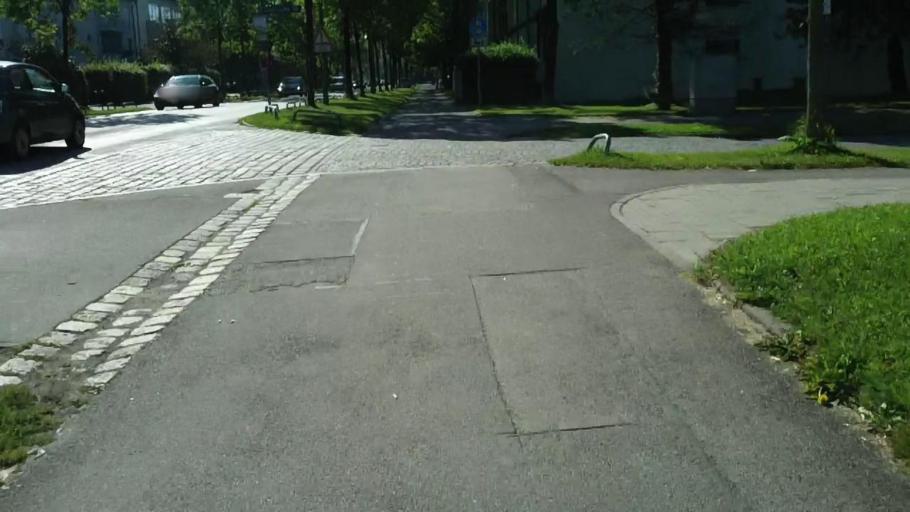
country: DE
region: Bavaria
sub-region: Upper Bavaria
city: Karlsfeld
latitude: 48.1881
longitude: 11.5033
